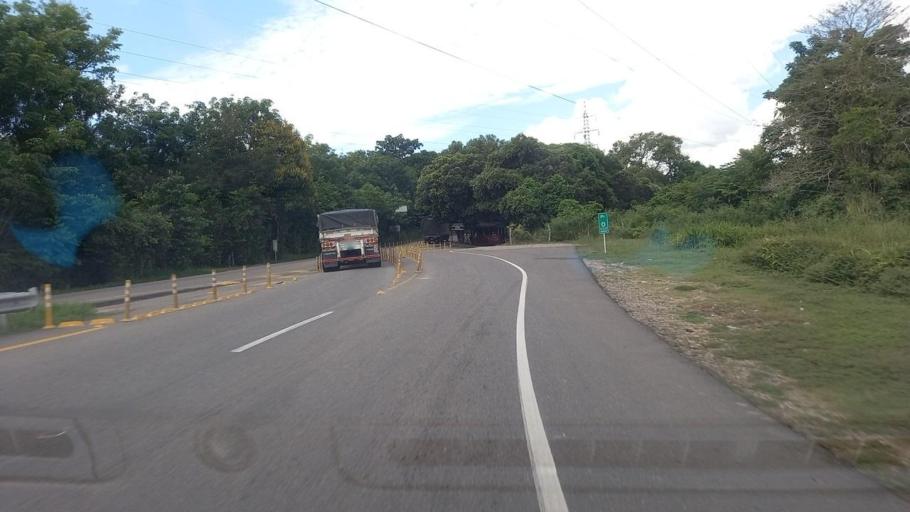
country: CO
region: Santander
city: Sabana de Torres
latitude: 7.1320
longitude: -73.5590
